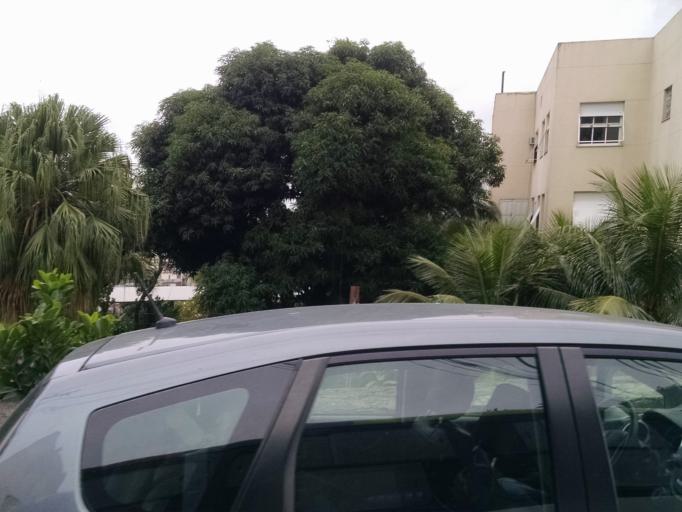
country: BR
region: Rio de Janeiro
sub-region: Rio De Janeiro
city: Rio de Janeiro
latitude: -22.9237
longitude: -43.1875
